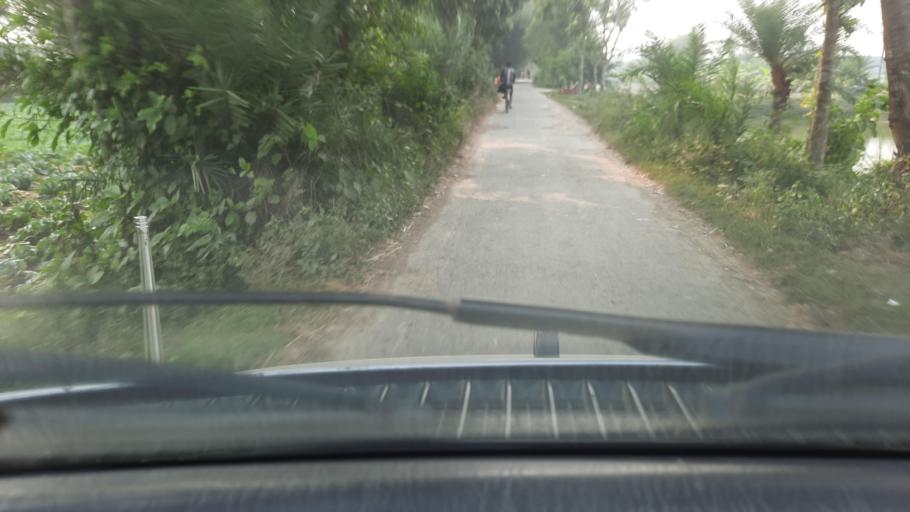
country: BD
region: Khulna
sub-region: Chuadanga
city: Nowlamary
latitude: 23.6003
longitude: 88.8498
